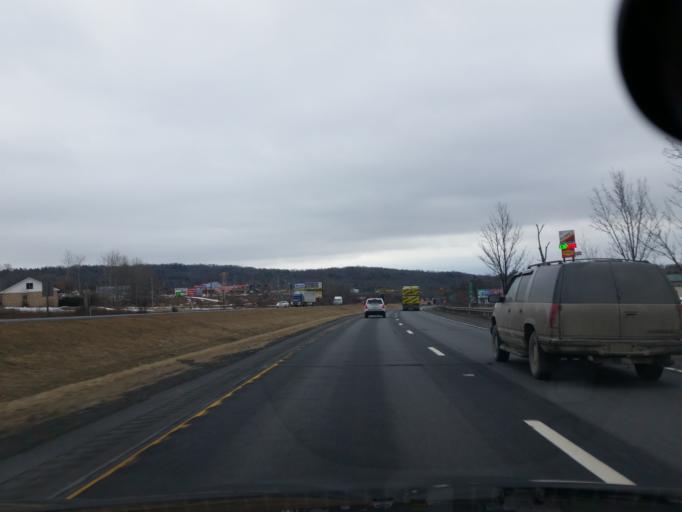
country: US
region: Pennsylvania
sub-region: Susquehanna County
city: Susquehanna
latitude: 41.8281
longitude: -75.6802
